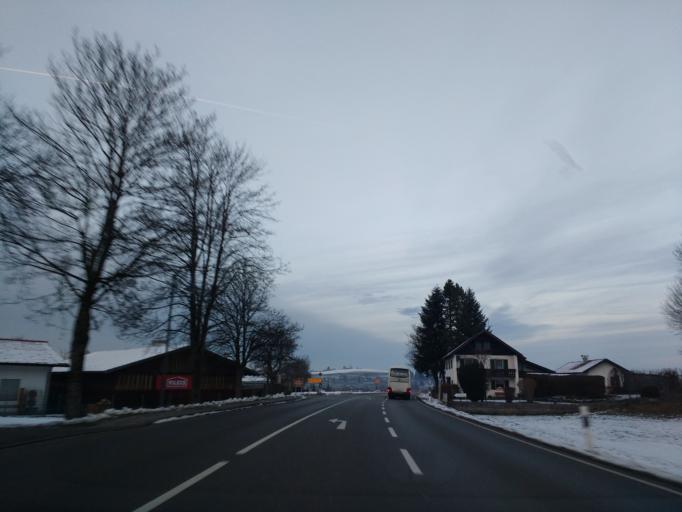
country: DE
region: Bavaria
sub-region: Swabia
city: Halblech
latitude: 47.6320
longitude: 10.8209
